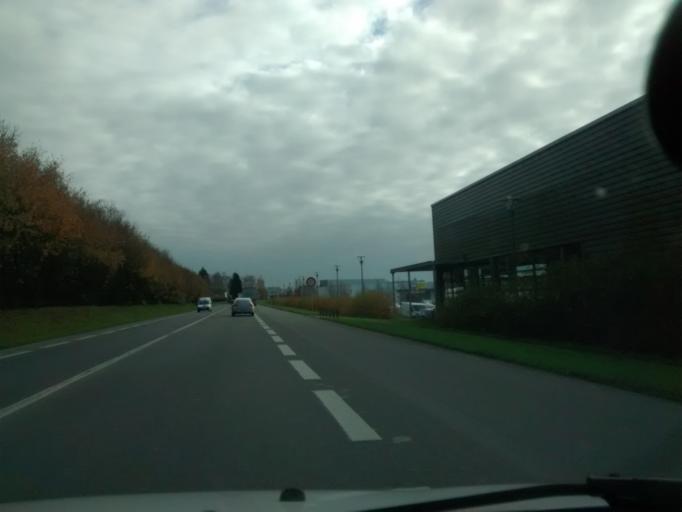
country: FR
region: Brittany
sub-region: Departement d'Ille-et-Vilaine
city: Vitre
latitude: 48.1111
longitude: -1.2182
